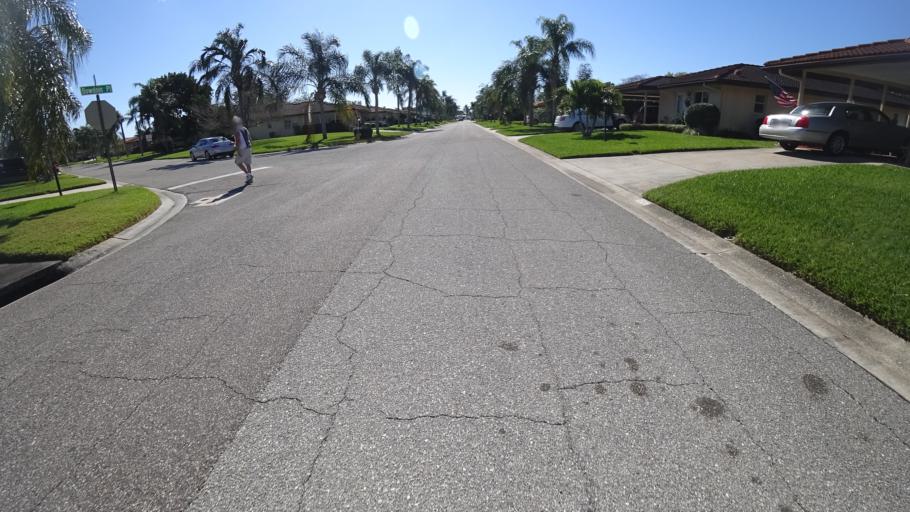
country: US
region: Florida
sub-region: Manatee County
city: Bayshore Gardens
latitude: 27.4257
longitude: -82.5946
